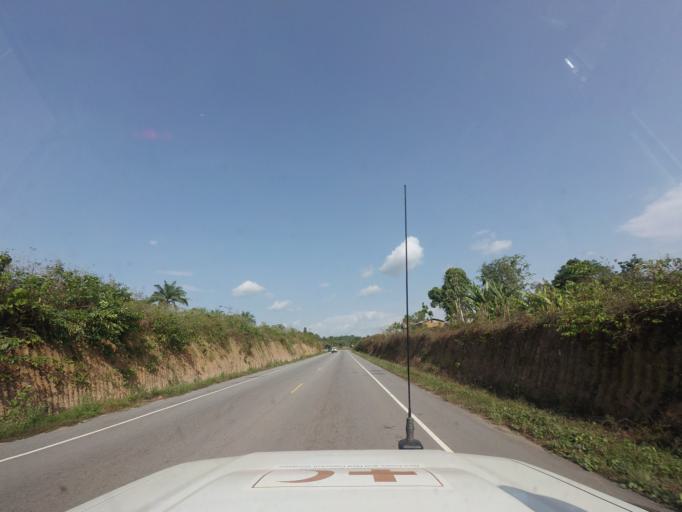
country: LR
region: Bong
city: Gbarnga
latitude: 6.8164
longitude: -9.8993
